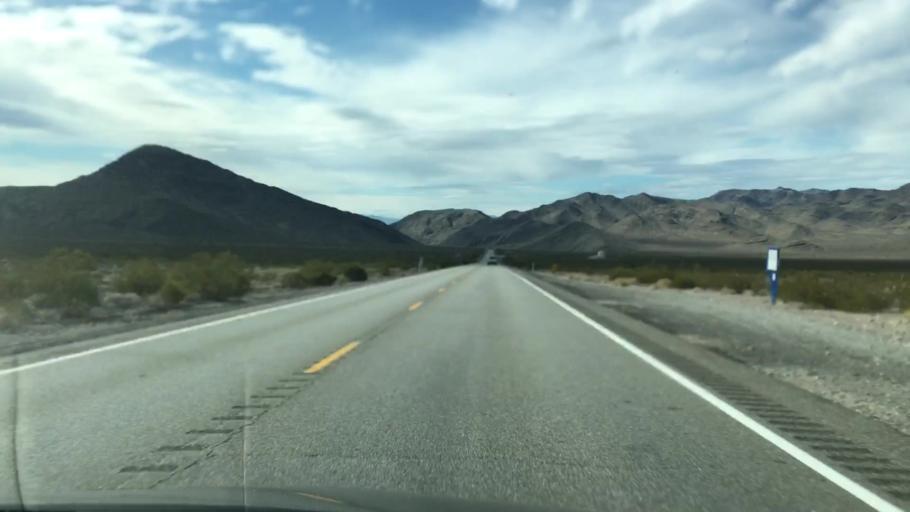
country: US
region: Nevada
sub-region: Nye County
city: Pahrump
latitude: 36.5925
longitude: -116.0280
